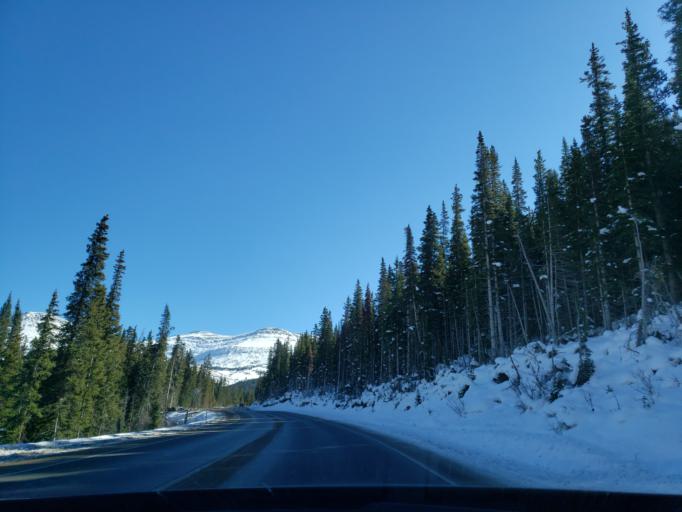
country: US
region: Colorado
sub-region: Summit County
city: Breckenridge
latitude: 39.3804
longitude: -106.0639
